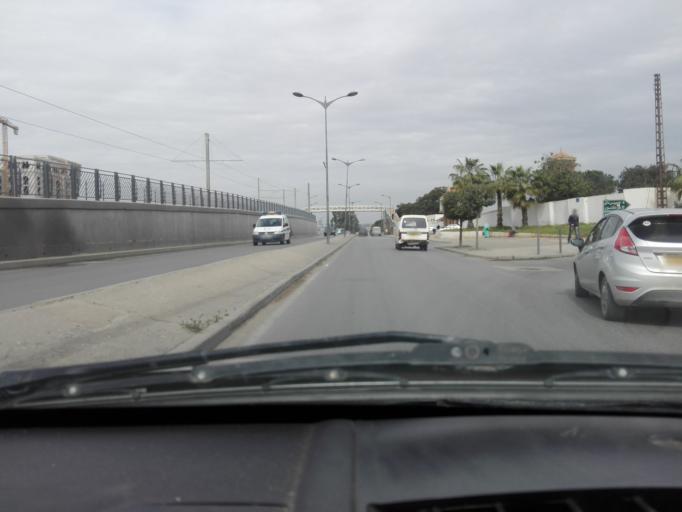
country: DZ
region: Alger
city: Bab Ezzouar
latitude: 36.7355
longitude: 3.1200
